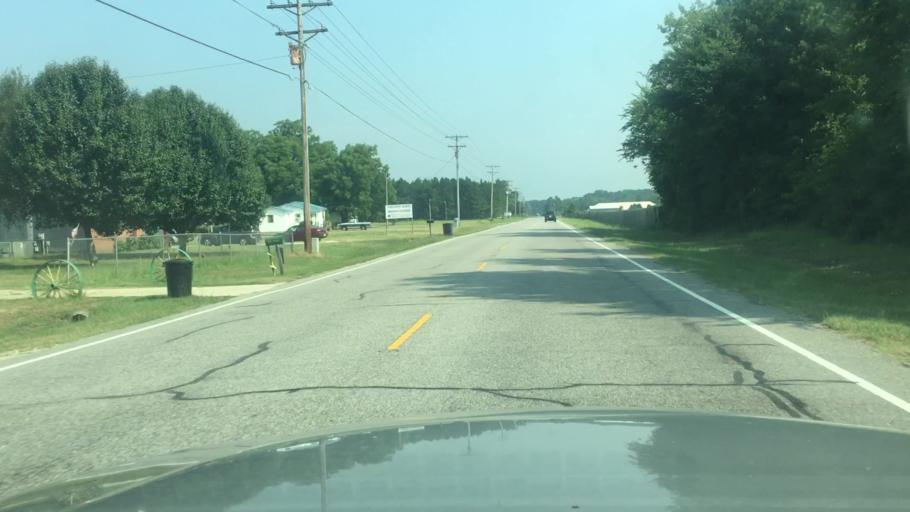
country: US
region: North Carolina
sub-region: Cumberland County
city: Hope Mills
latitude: 34.9006
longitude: -78.9007
